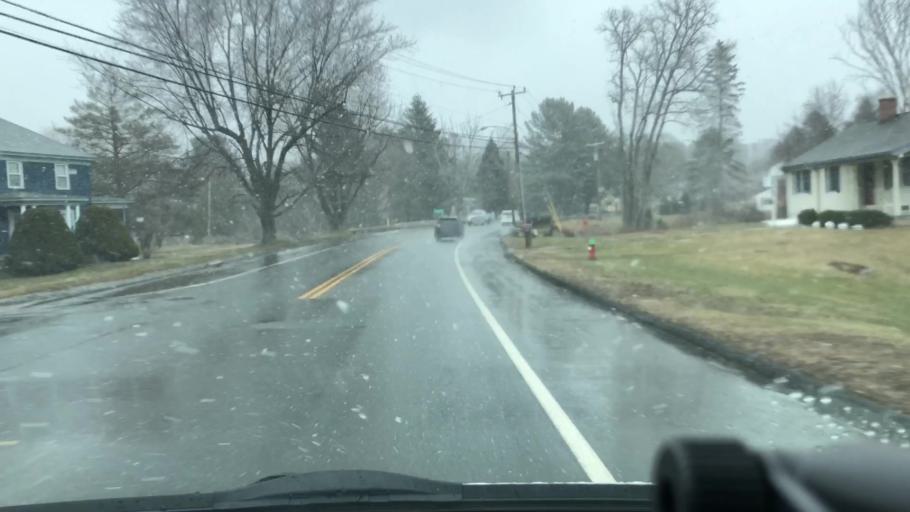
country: US
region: Massachusetts
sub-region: Berkshire County
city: Dalton
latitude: 42.4840
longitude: -73.1495
